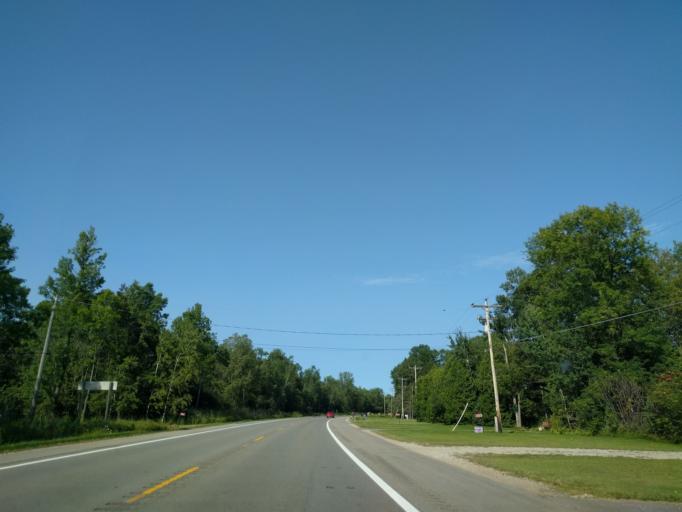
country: US
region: Michigan
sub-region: Menominee County
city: Menominee
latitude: 45.1668
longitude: -87.5866
